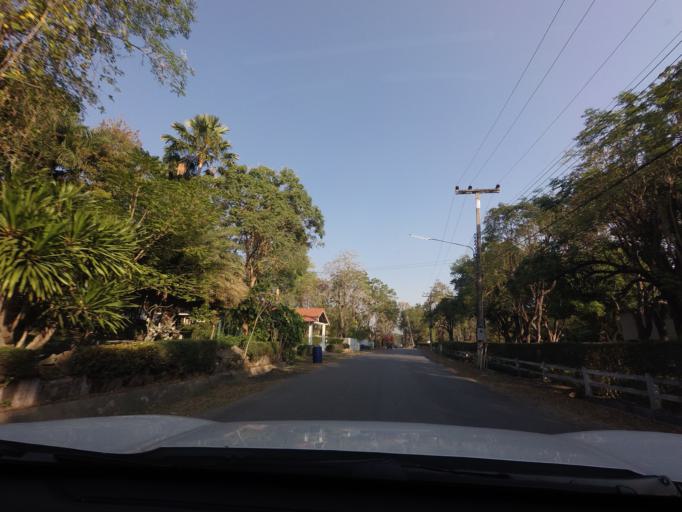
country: TH
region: Nakhon Ratchasima
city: Pak Chong
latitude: 14.5864
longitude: 101.4451
